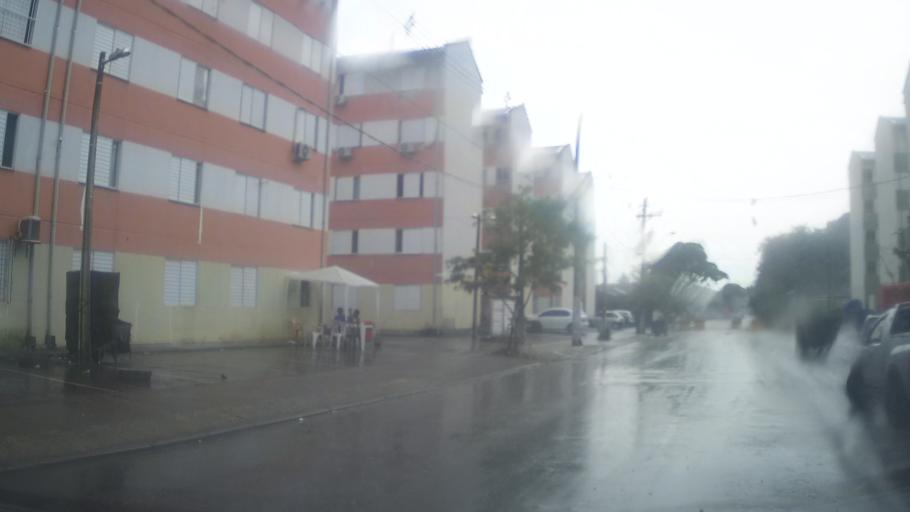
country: BR
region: Sao Paulo
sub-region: Santos
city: Santos
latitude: -23.9433
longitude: -46.3629
